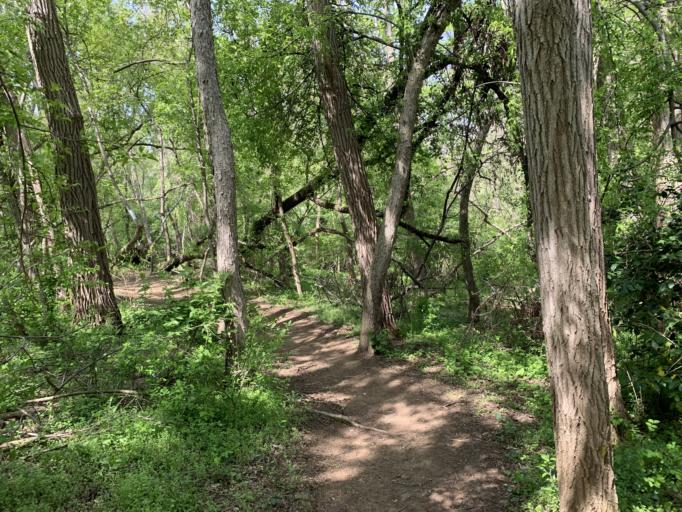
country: US
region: Pennsylvania
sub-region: Delaware County
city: Lima
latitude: 39.9531
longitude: -75.4434
